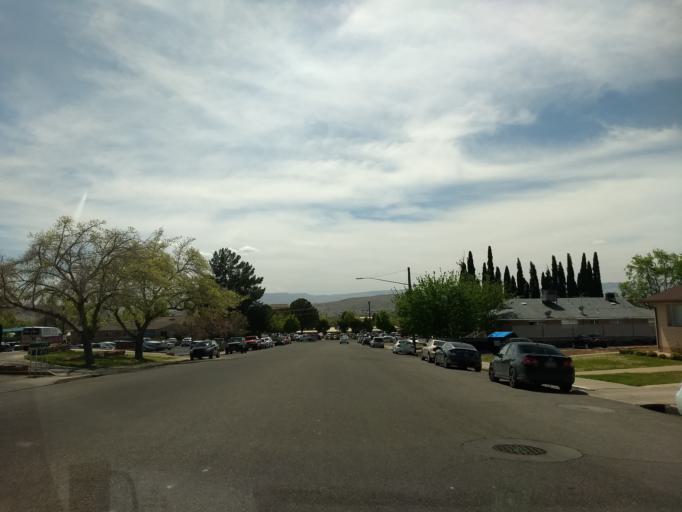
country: US
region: Utah
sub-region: Washington County
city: Saint George
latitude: 37.1078
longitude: -113.5664
